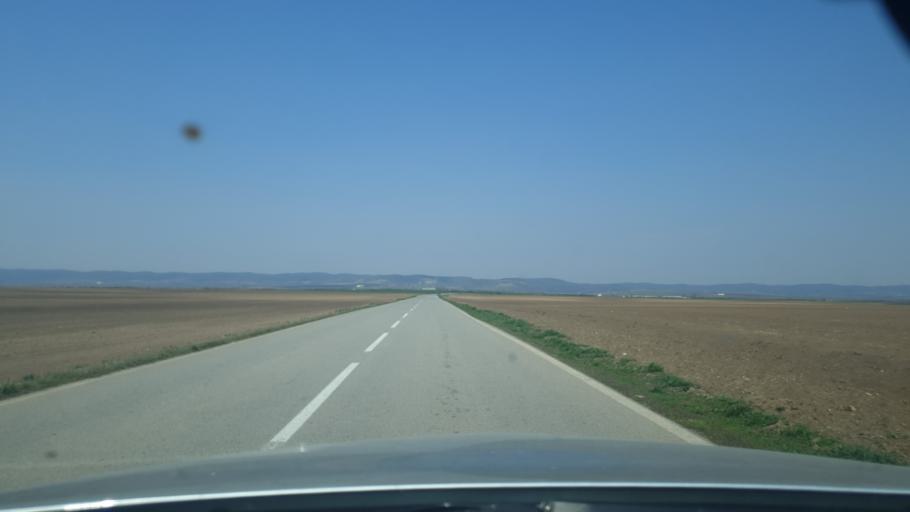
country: RS
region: Autonomna Pokrajina Vojvodina
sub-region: Sremski Okrug
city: Ruma
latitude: 45.0387
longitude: 19.7615
